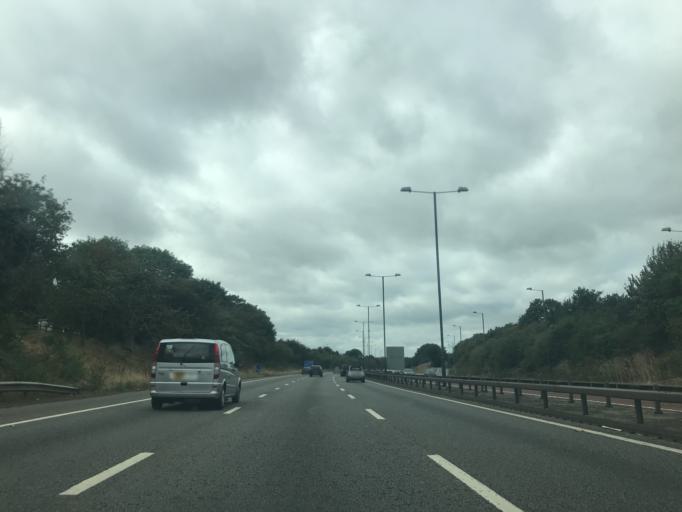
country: GB
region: England
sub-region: Greater London
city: Southall
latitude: 51.4881
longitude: -0.3811
